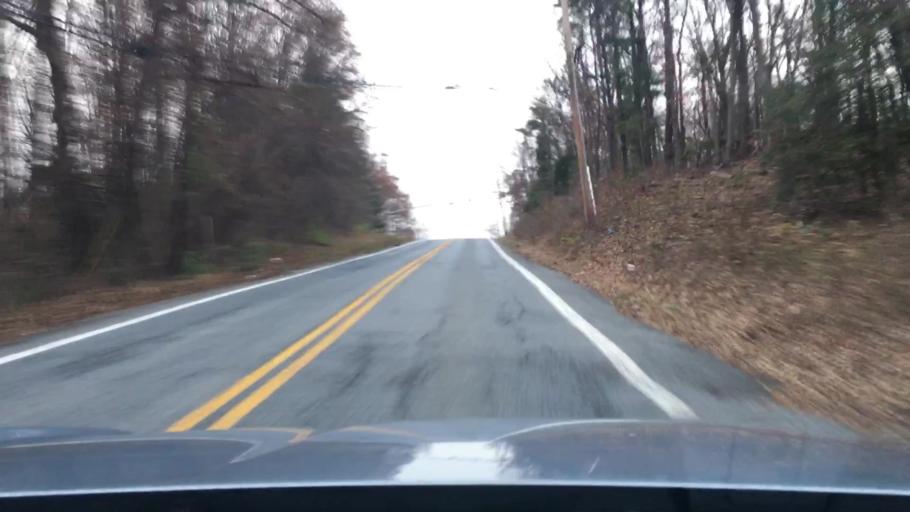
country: US
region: Maryland
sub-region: Prince George's County
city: Glenn Dale
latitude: 39.0194
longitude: -76.7848
